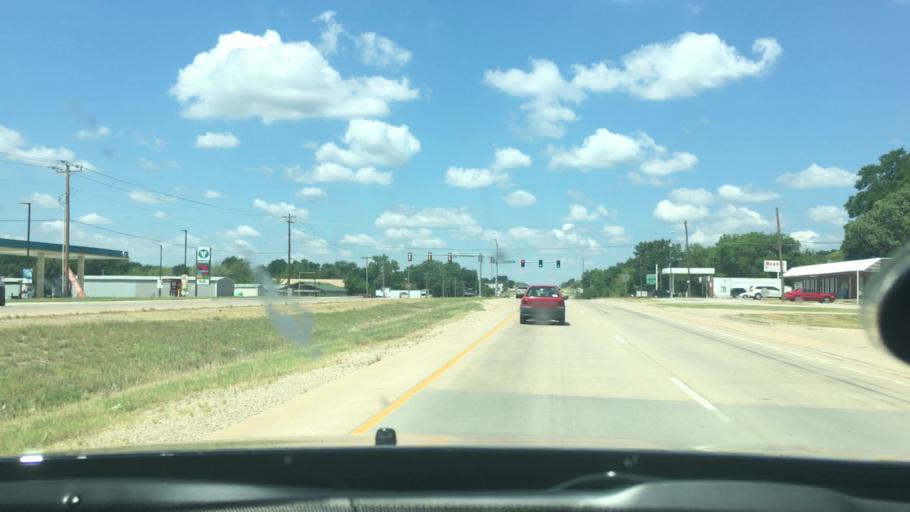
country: US
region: Oklahoma
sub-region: Carter County
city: Lone Grove
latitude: 34.1730
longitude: -97.2288
